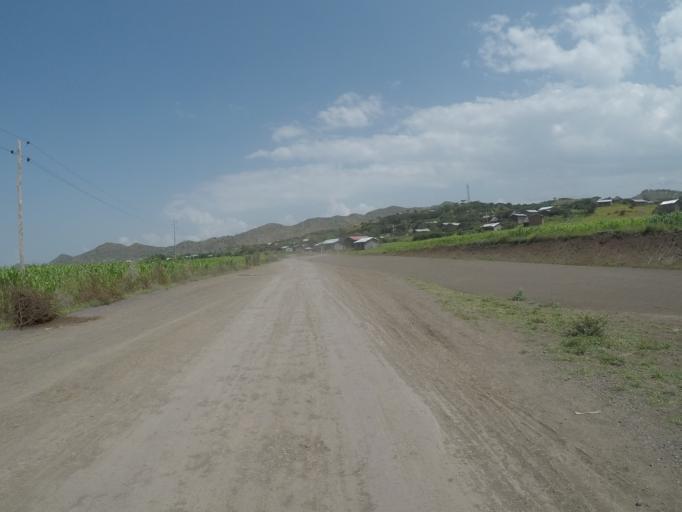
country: ET
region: Amhara
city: Lalibela
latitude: 11.9790
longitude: 38.9878
